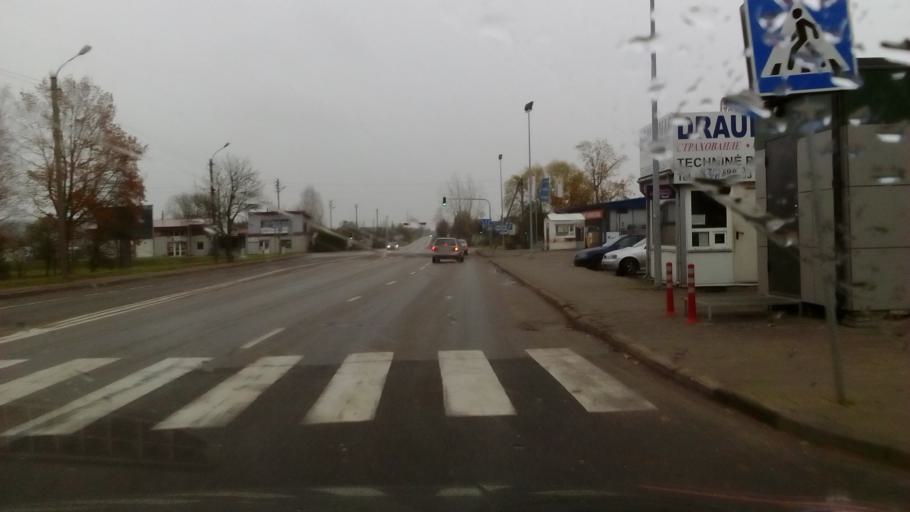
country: LT
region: Marijampoles apskritis
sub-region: Marijampole Municipality
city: Marijampole
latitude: 54.5539
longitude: 23.3723
